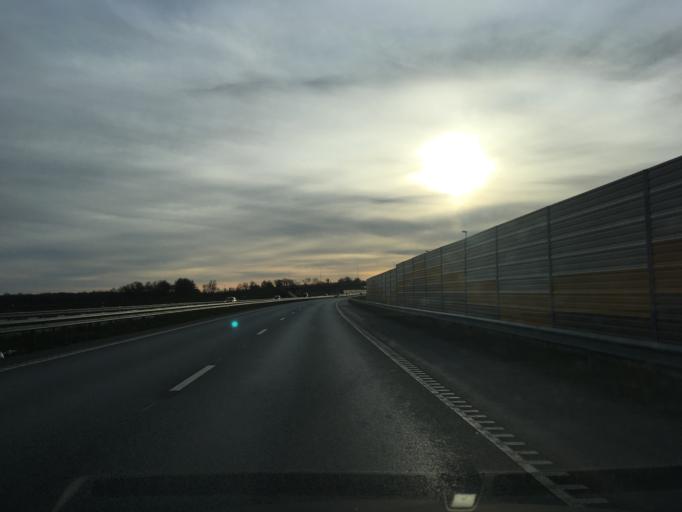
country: EE
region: Ida-Virumaa
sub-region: Johvi vald
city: Johvi
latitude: 59.3778
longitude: 27.3754
